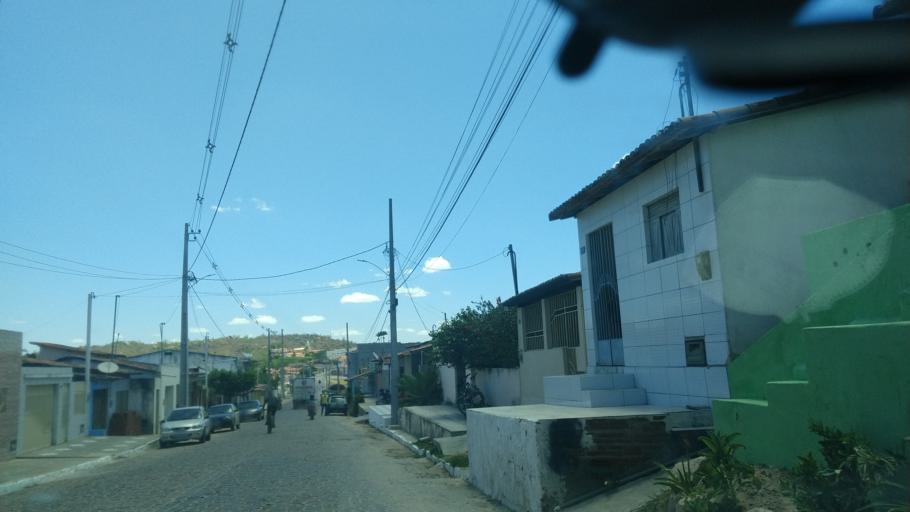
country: BR
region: Rio Grande do Norte
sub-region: Cerro Cora
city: Cerro Cora
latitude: -6.0387
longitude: -36.3469
